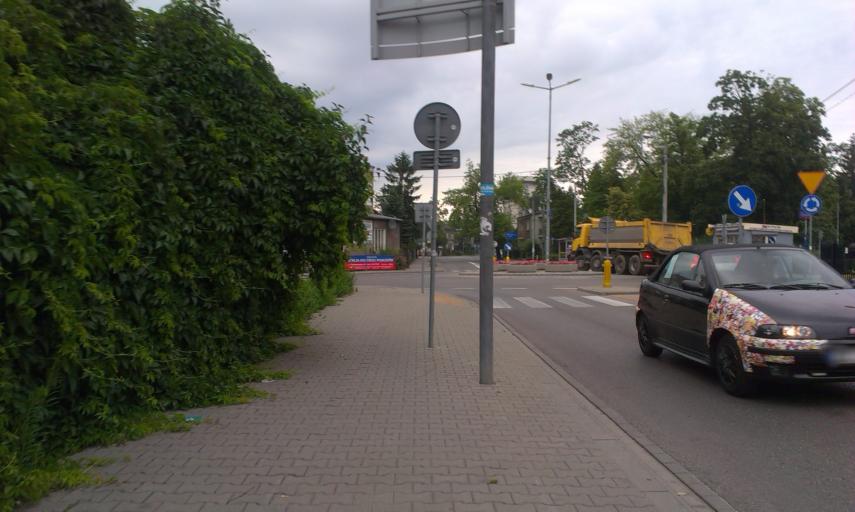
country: PL
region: Masovian Voivodeship
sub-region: Warszawa
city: Ursus
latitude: 52.1944
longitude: 20.8843
